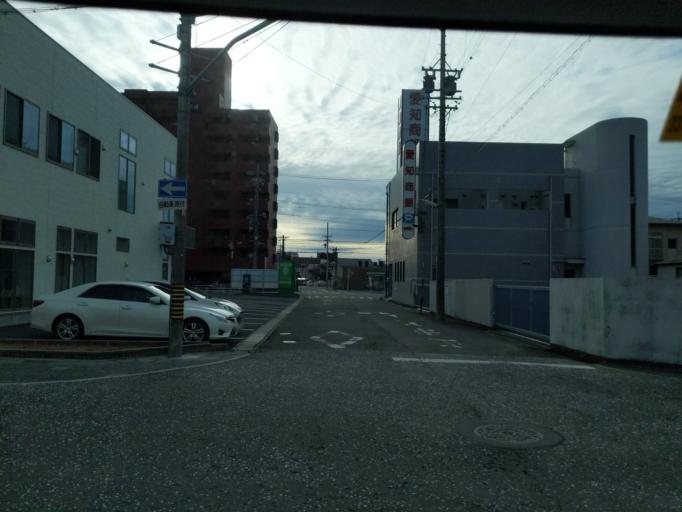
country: JP
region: Aichi
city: Kasugai
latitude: 35.2514
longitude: 136.9812
